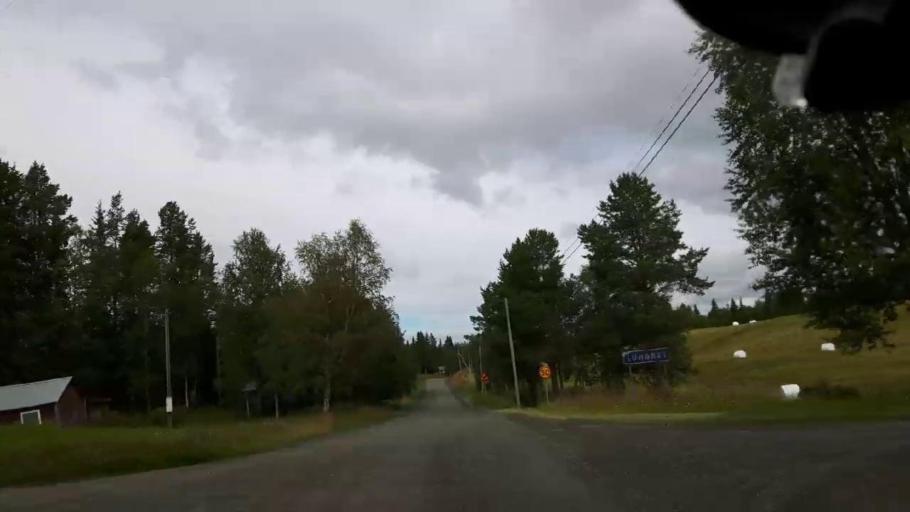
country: SE
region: Jaemtland
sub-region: Krokoms Kommun
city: Valla
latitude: 63.4098
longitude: 14.0904
